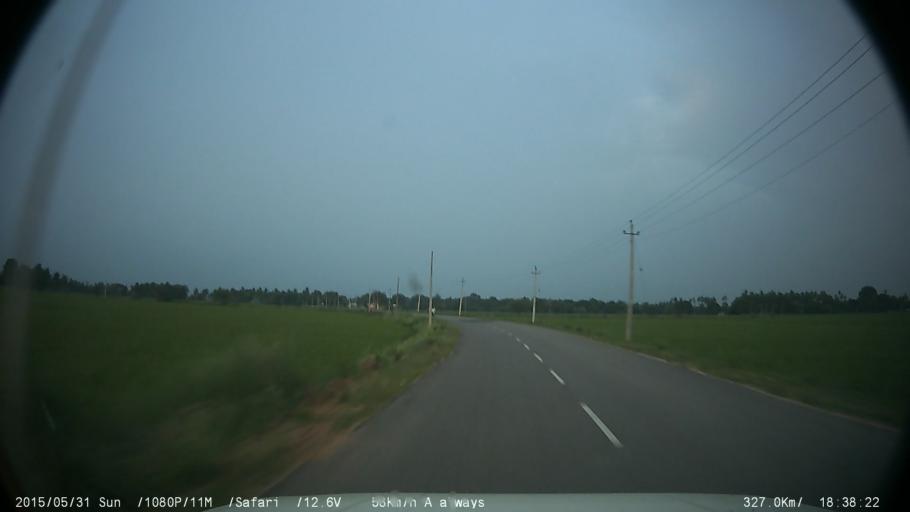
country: IN
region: Karnataka
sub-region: Mysore
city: Nanjangud
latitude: 12.1445
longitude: 76.7772
